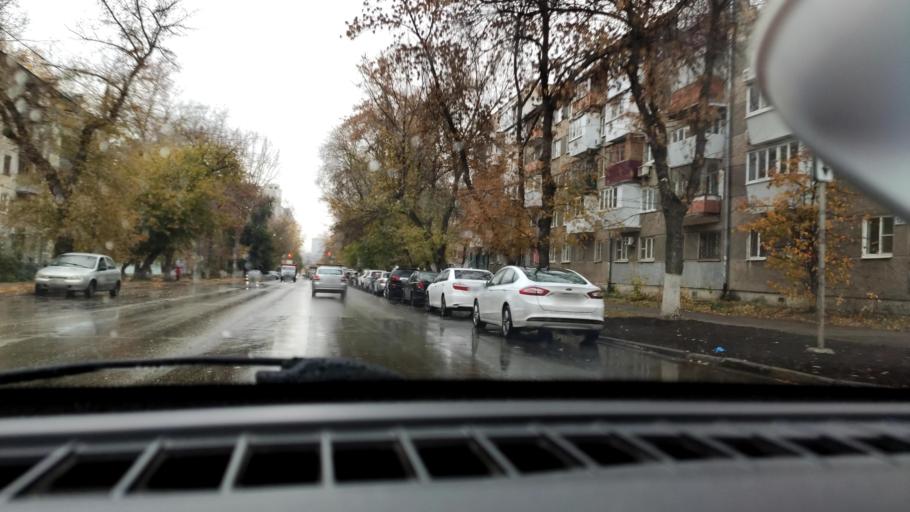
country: RU
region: Samara
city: Samara
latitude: 53.2130
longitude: 50.1603
